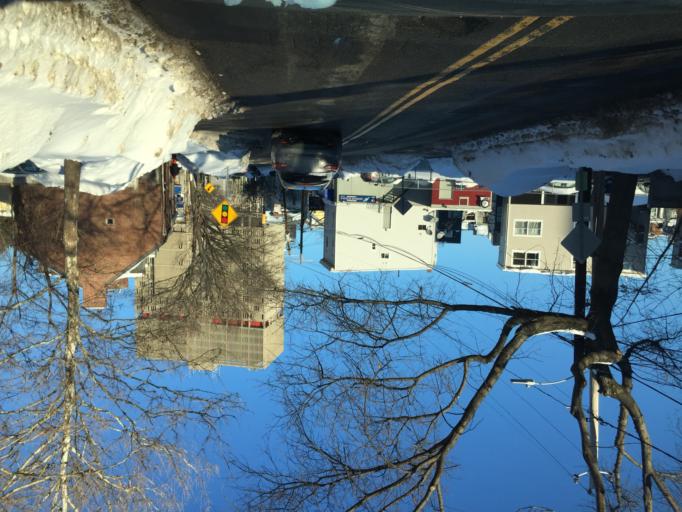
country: US
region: Massachusetts
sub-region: Suffolk County
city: Boston
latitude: 42.3671
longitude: -71.0816
